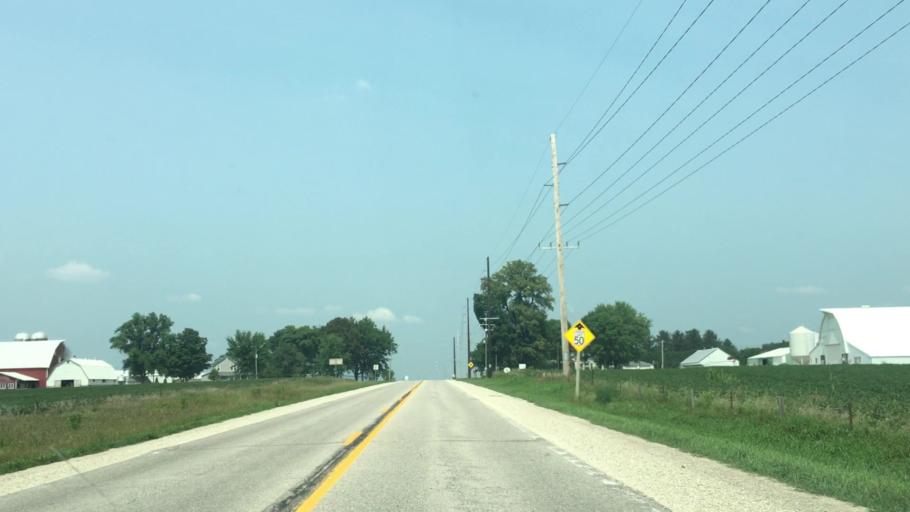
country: US
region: Iowa
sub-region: Buchanan County
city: Independence
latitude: 42.4404
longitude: -91.8900
